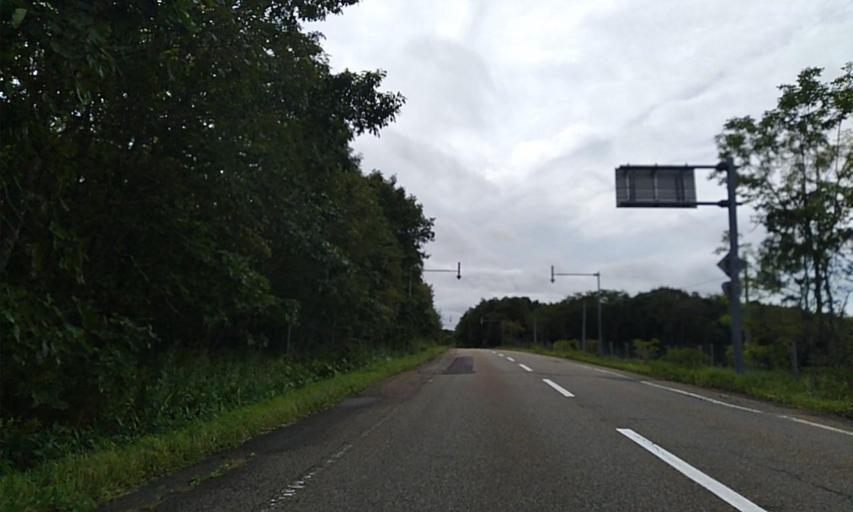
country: JP
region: Hokkaido
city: Shibetsu
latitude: 43.3502
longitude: 145.2153
